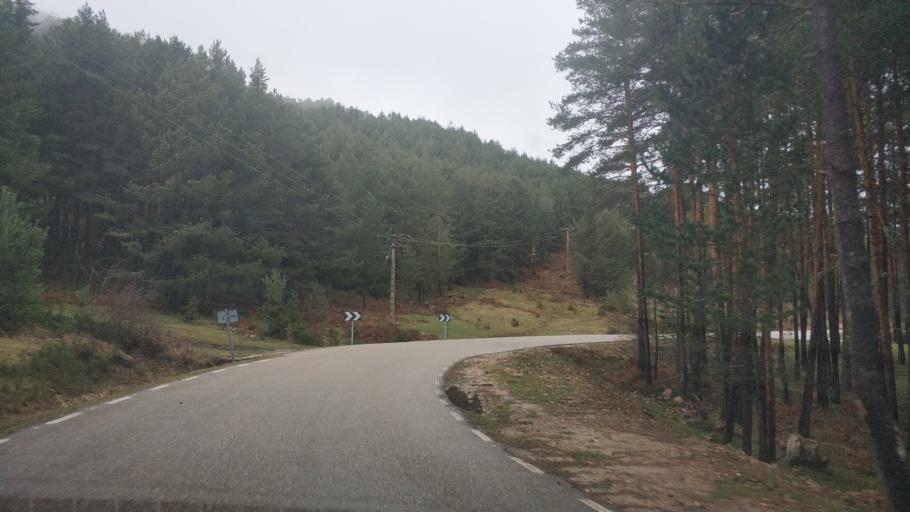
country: ES
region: Castille and Leon
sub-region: Provincia de Burgos
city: Neila
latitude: 42.0239
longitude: -3.0137
